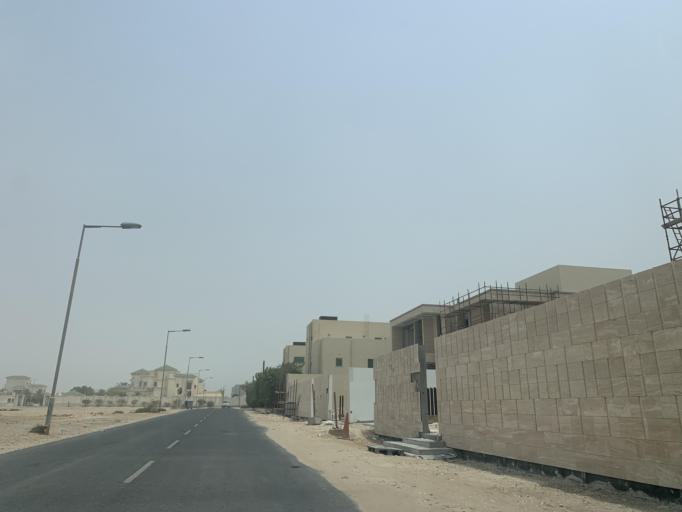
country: BH
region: Central Governorate
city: Madinat Hamad
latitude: 26.1697
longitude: 50.4772
